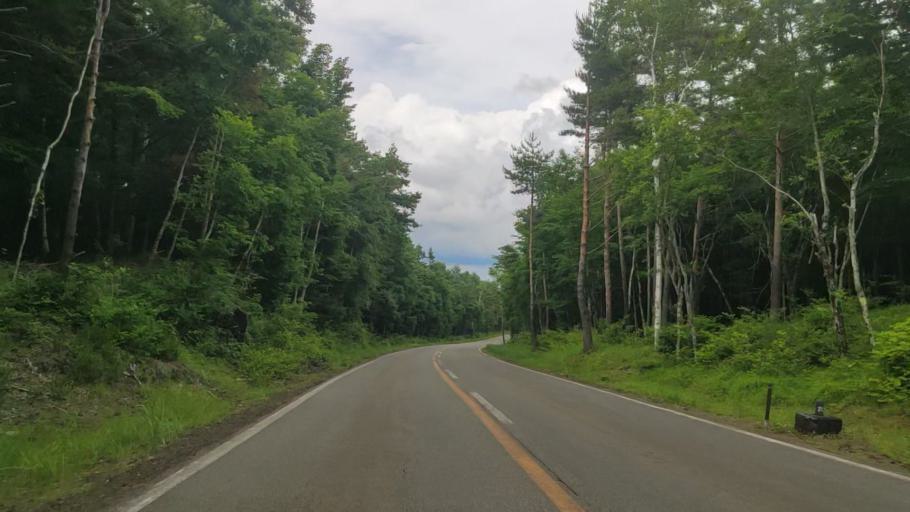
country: JP
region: Yamanashi
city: Fujikawaguchiko
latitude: 35.4338
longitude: 138.7379
